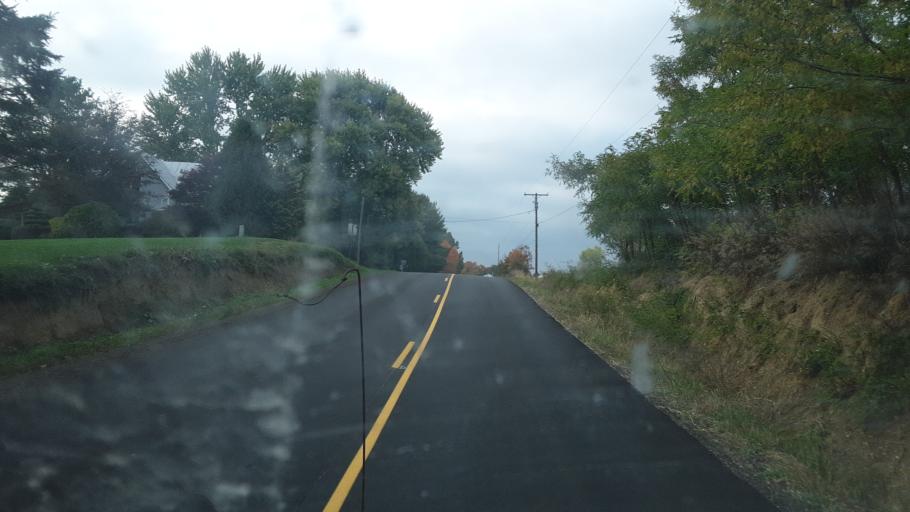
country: US
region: Ohio
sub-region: Ashland County
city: Ashland
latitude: 40.7707
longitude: -82.2379
